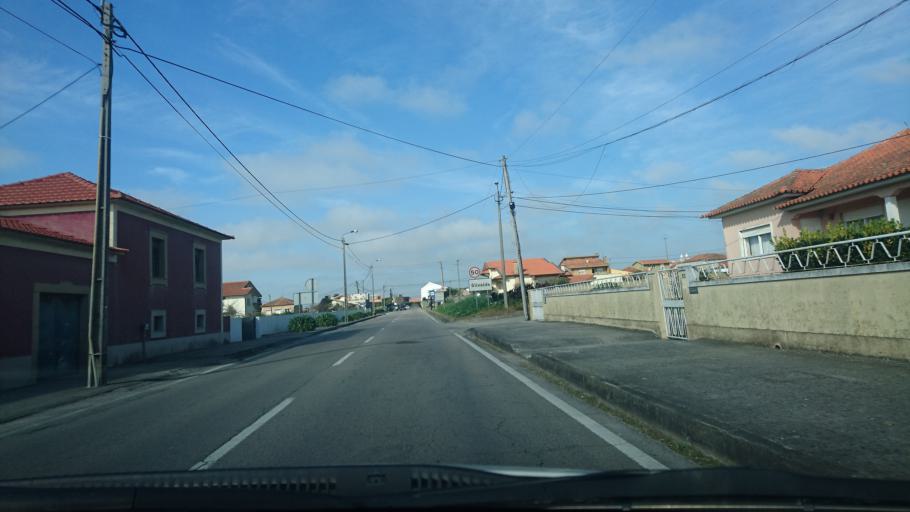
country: PT
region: Aveiro
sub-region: Espinho
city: Souto
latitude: 40.9837
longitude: -8.6321
